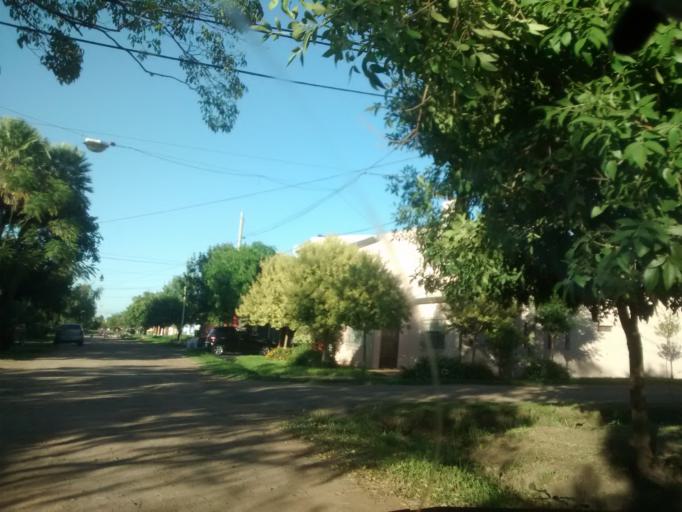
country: AR
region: Chaco
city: Resistencia
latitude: -27.4501
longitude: -59.0029
